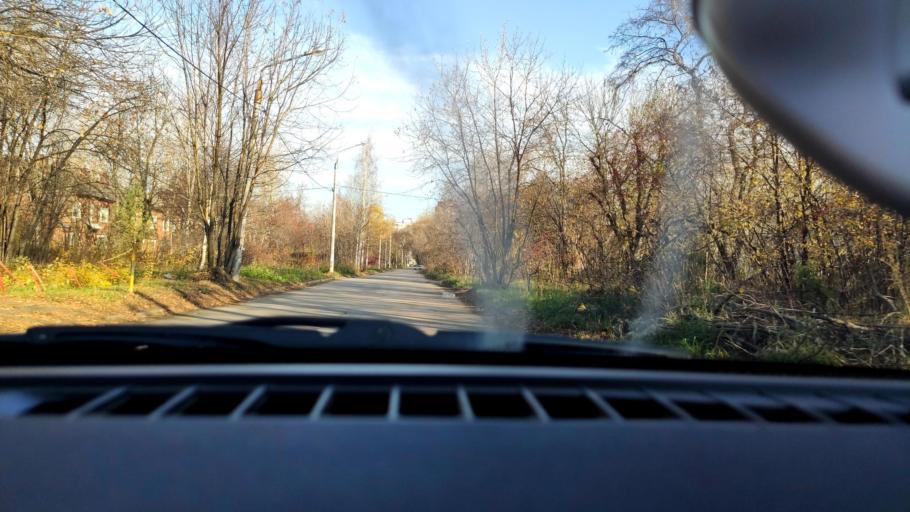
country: RU
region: Perm
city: Perm
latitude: 57.9594
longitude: 56.2350
